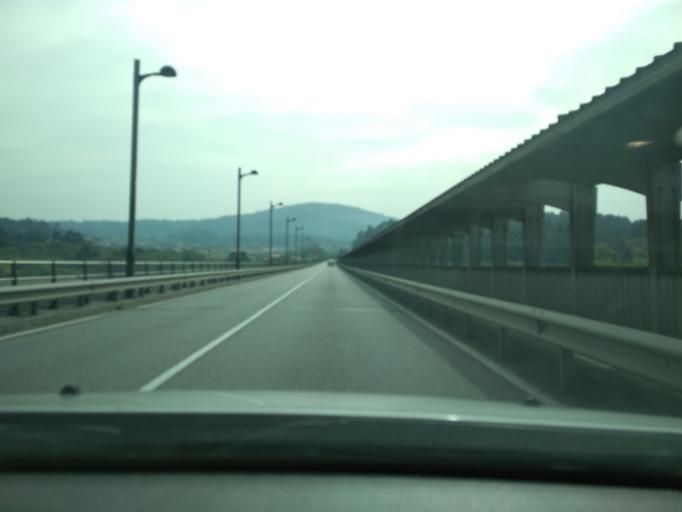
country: ES
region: Galicia
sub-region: Provincia de Pontevedra
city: Catoira
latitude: 42.6770
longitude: -8.7246
